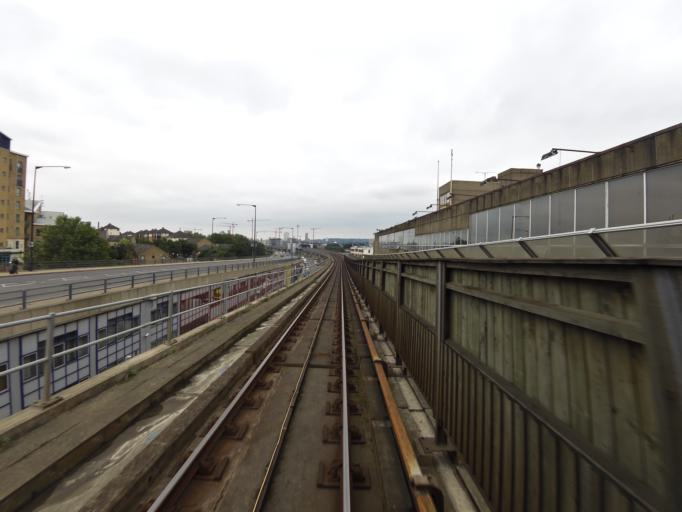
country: GB
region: England
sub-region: Greater London
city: Poplar
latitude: 51.5052
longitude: 0.0166
